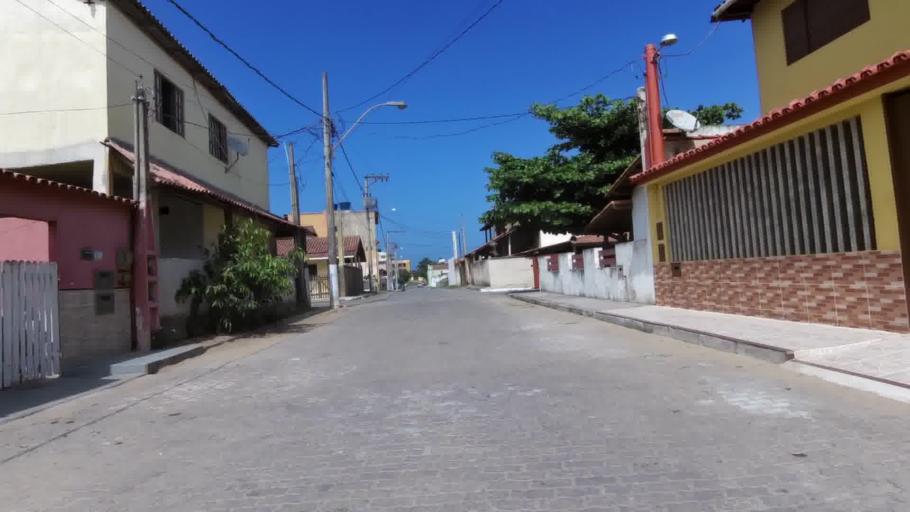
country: BR
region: Espirito Santo
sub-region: Marataizes
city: Marataizes
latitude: -21.0312
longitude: -40.8134
